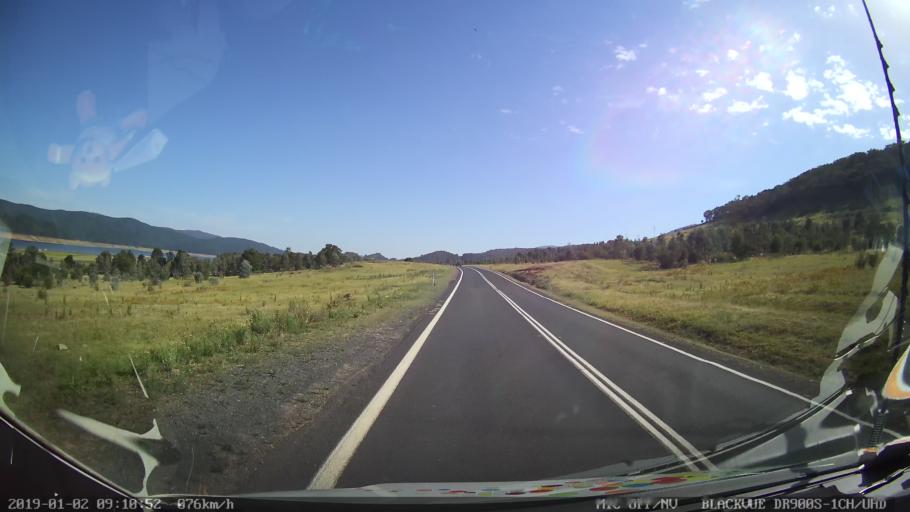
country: AU
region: New South Wales
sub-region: Tumut Shire
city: Tumut
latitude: -35.5176
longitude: 148.2685
